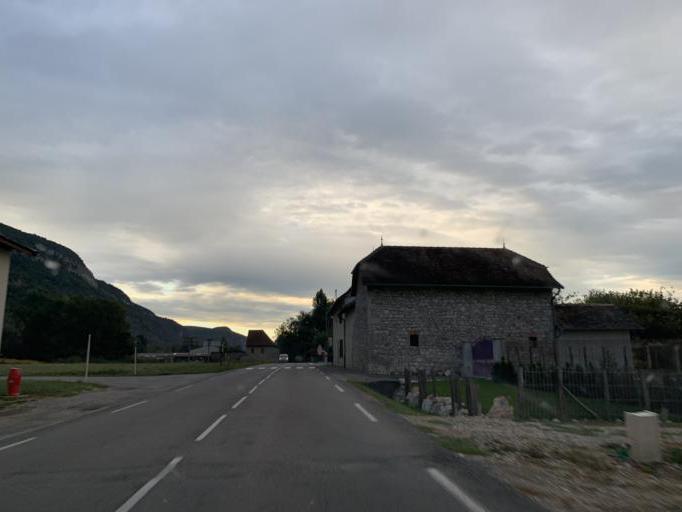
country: FR
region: Rhone-Alpes
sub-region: Departement de l'Isere
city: Les Avenieres
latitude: 45.6926
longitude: 5.5887
